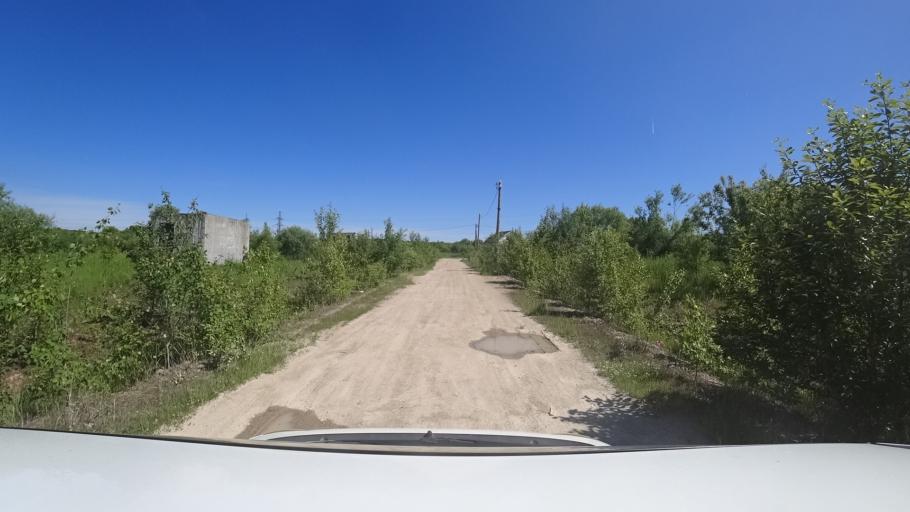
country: RU
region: Khabarovsk Krai
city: Topolevo
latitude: 48.5649
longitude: 135.1935
